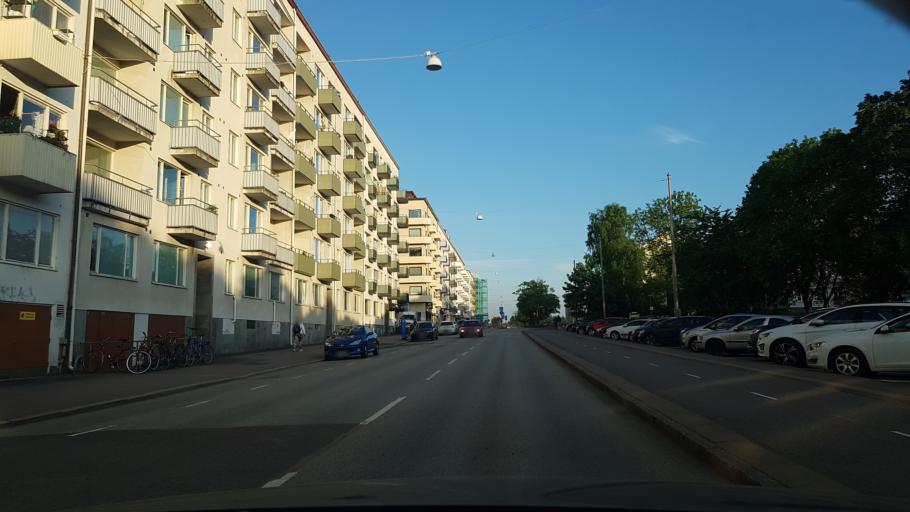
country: SE
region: Vaestra Goetaland
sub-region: Goteborg
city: Goeteborg
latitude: 57.6885
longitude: 11.9815
